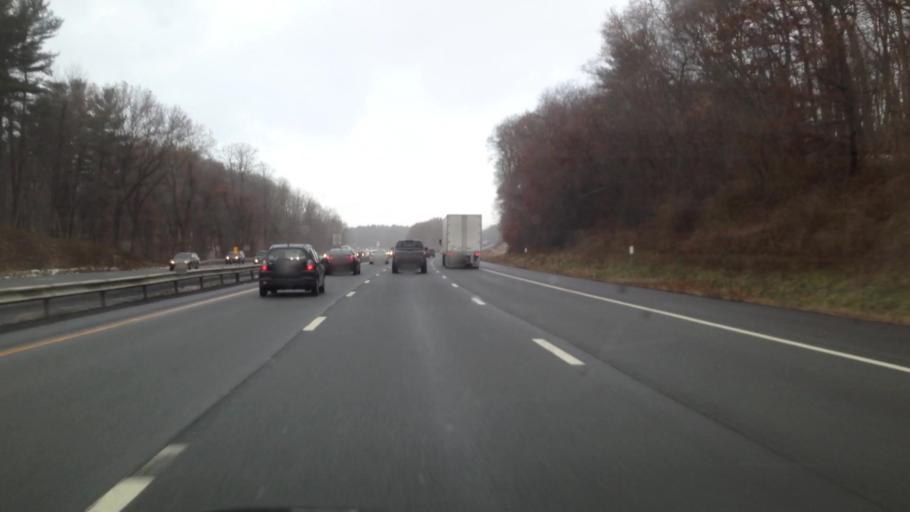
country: US
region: New York
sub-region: Albany County
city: Westmere
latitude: 42.7386
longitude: -73.9082
